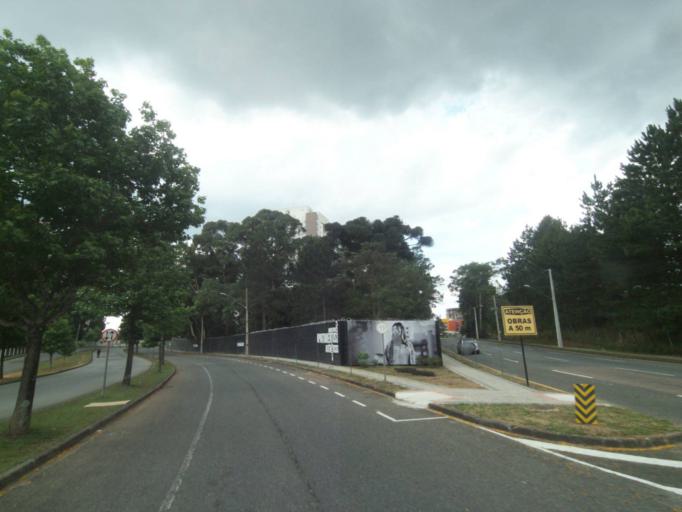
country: BR
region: Parana
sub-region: Curitiba
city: Curitiba
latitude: -25.4483
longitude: -49.3535
